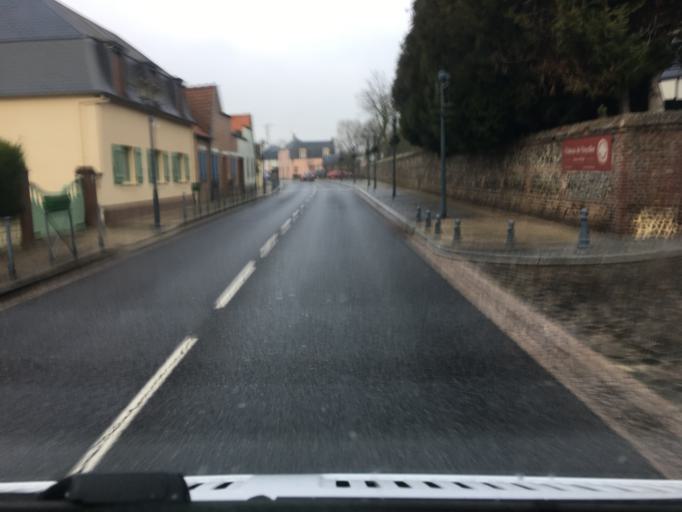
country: FR
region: Picardie
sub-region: Departement de la Somme
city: Sailly-Flibeaucourt
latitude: 50.1857
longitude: 1.7068
